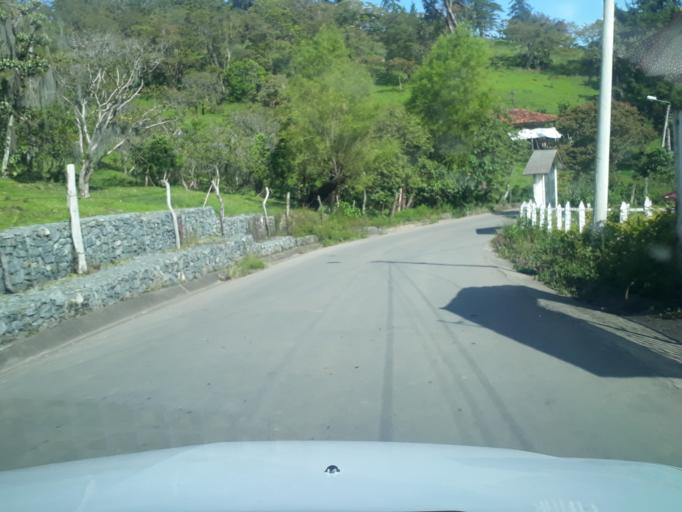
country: CO
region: Santander
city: Velez
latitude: 6.0229
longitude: -73.6649
